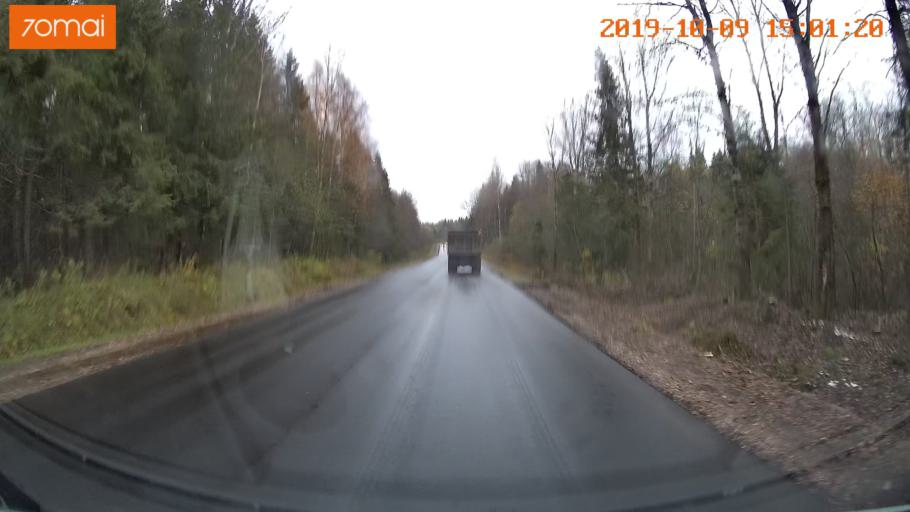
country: RU
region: Kostroma
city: Chistyye Bory
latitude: 58.2977
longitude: 41.6804
